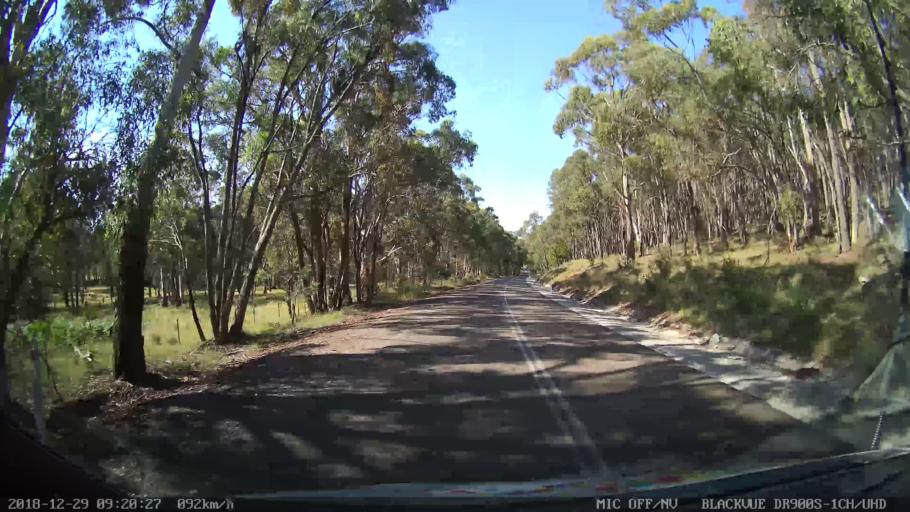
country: AU
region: New South Wales
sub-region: Upper Lachlan Shire
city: Crookwell
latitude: -34.4930
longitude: 149.4243
